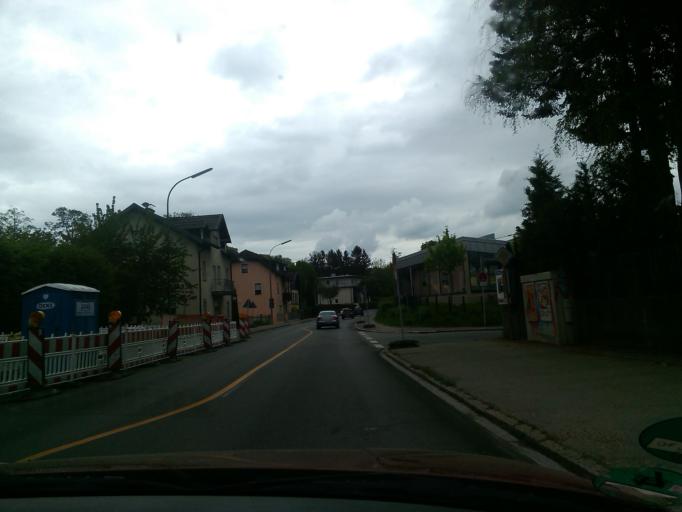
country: DE
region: Bavaria
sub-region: Upper Bavaria
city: Grafelfing
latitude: 48.1178
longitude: 11.4394
